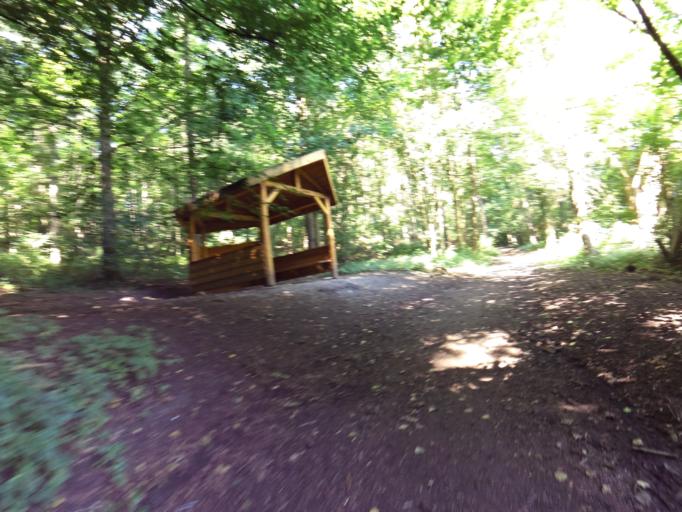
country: DE
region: North Rhine-Westphalia
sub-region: Regierungsbezirk Koln
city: Herzogenrath
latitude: 50.8392
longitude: 6.0960
